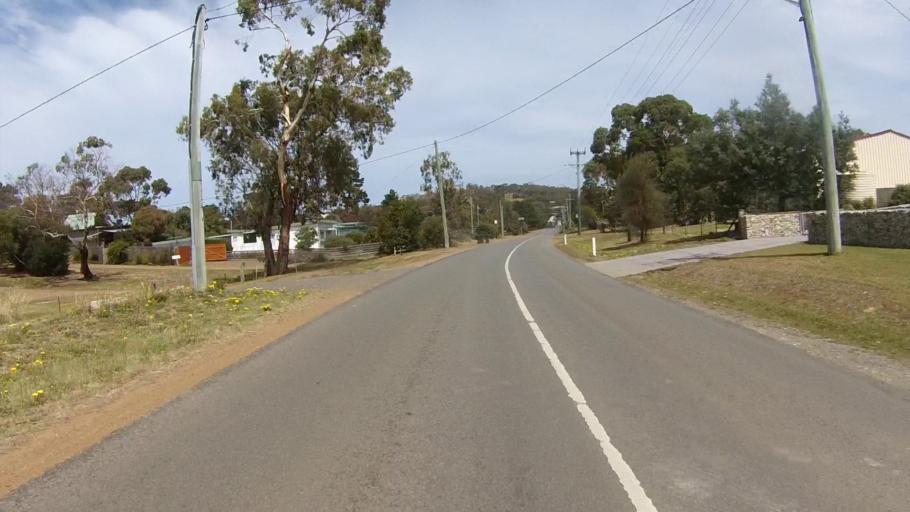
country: AU
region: Tasmania
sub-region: Kingborough
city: Blackmans Bay
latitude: -43.0239
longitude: 147.4180
